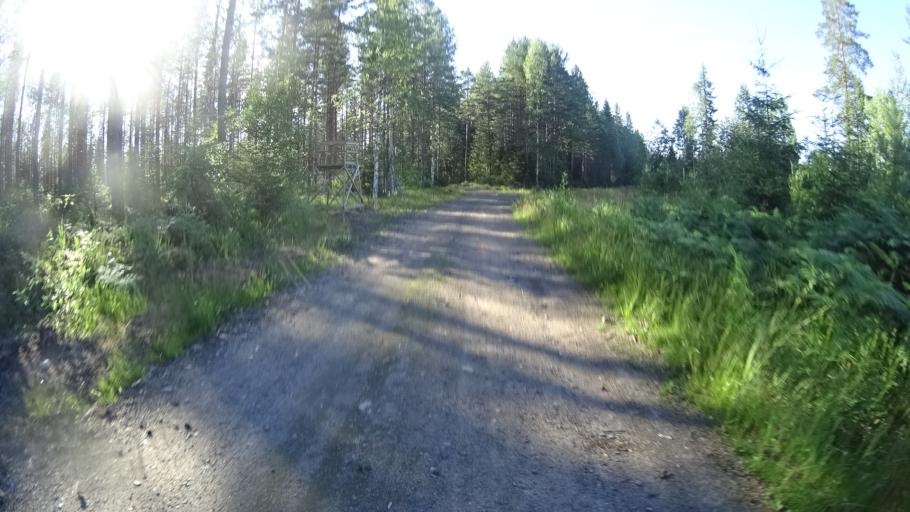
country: FI
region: Uusimaa
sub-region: Helsinki
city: Karkkila
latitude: 60.6575
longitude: 24.1315
